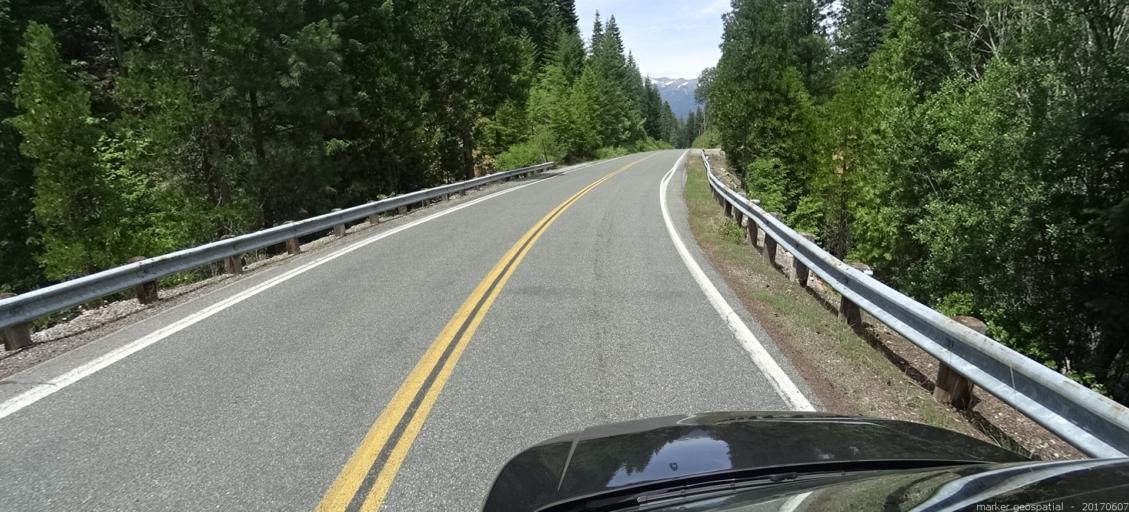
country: US
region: California
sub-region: Siskiyou County
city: Mount Shasta
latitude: 41.2700
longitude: -122.3384
